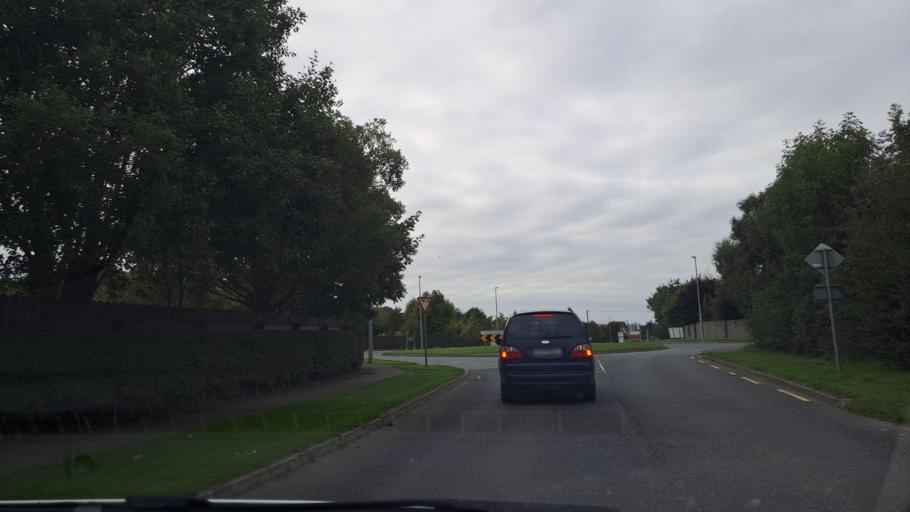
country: IE
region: Ulster
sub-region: County Monaghan
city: Carrickmacross
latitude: 53.9870
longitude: -6.7227
